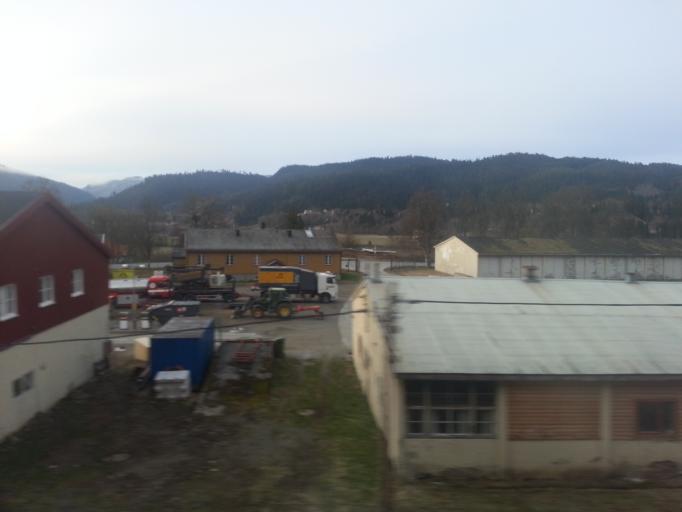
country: NO
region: Sor-Trondelag
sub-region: Midtre Gauldal
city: Storen
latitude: 63.0323
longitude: 10.2685
